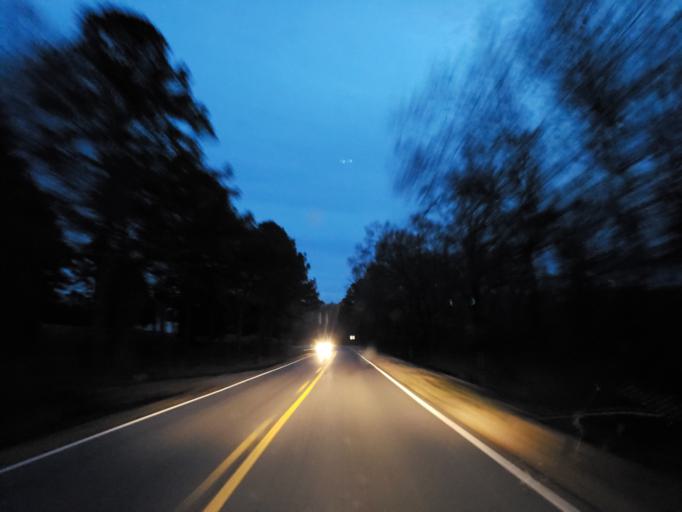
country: US
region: Alabama
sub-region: Greene County
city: Eutaw
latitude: 32.8726
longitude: -87.9282
